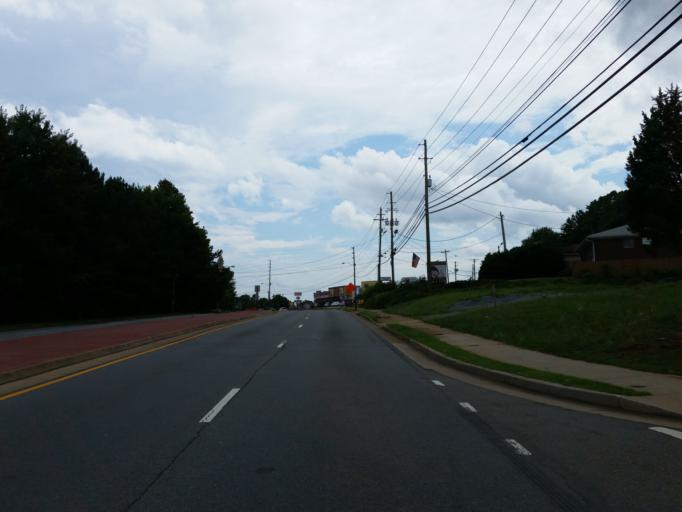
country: US
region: Georgia
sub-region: Cobb County
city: Kennesaw
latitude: 34.0635
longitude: -84.5916
